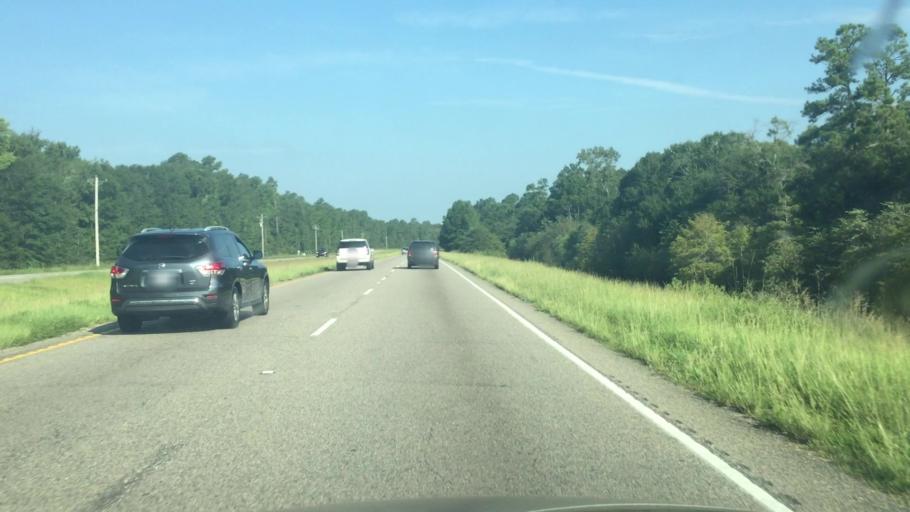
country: US
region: South Carolina
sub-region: Horry County
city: North Myrtle Beach
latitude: 33.9137
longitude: -78.7169
